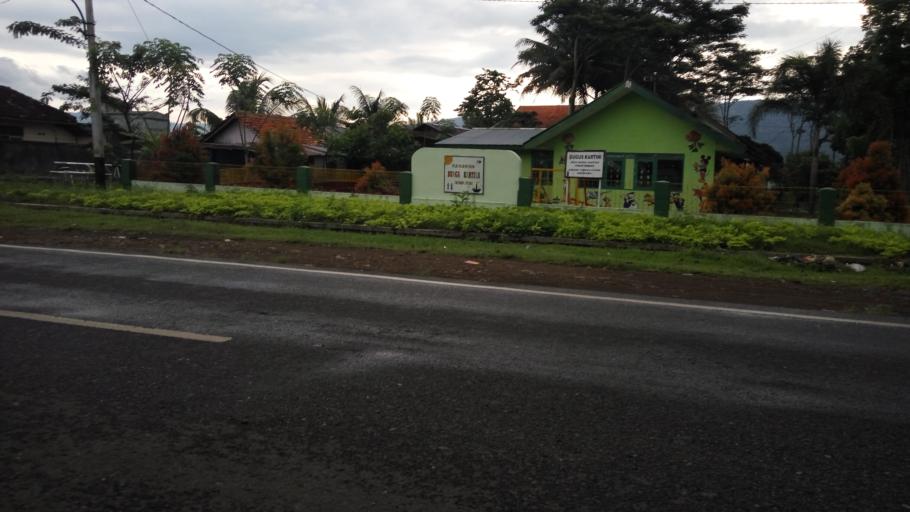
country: ID
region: Central Java
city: Ambarawa
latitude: -7.2696
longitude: 110.4026
